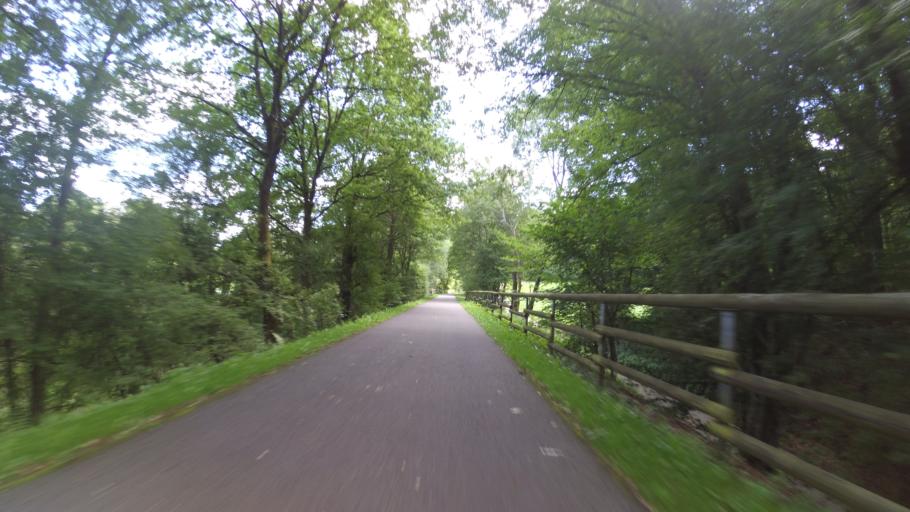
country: DE
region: Saarland
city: Namborn
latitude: 49.4937
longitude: 7.1304
